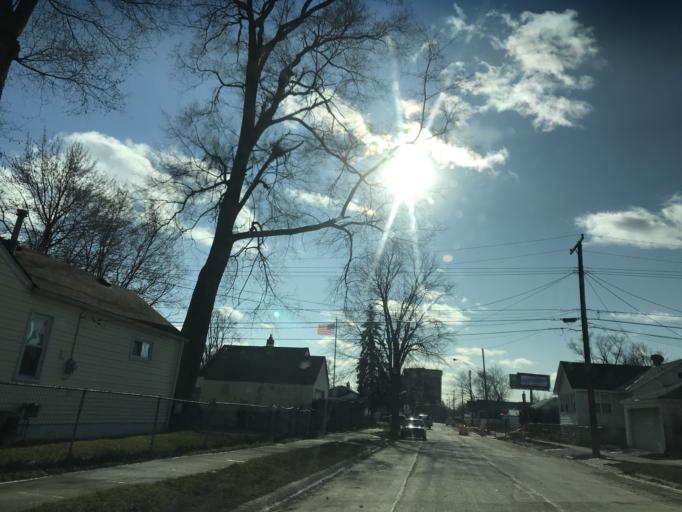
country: US
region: Michigan
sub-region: Oakland County
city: Hazel Park
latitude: 42.4679
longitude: -83.1066
